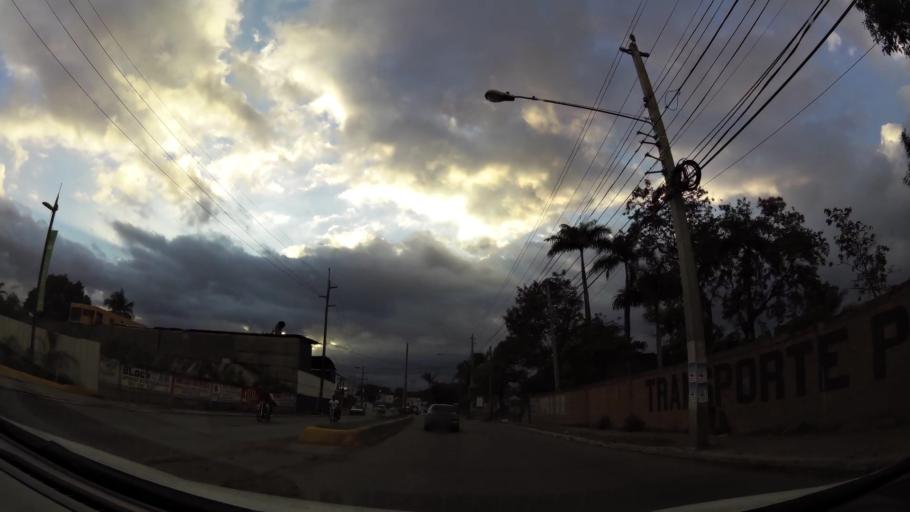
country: DO
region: Nacional
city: Santo Domingo
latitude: 18.5075
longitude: -69.9915
